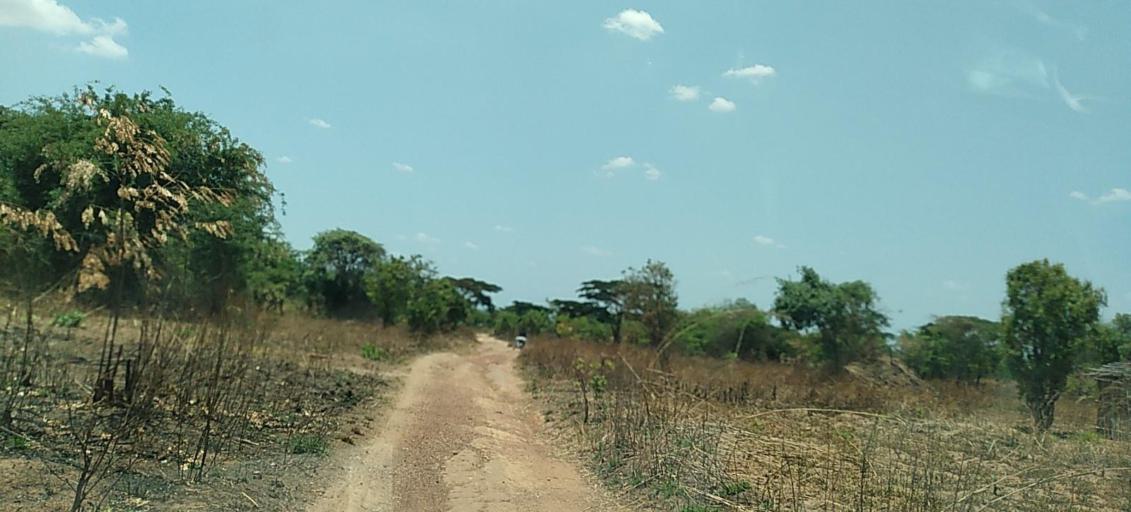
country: ZM
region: Copperbelt
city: Luanshya
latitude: -13.0675
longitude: 28.4051
